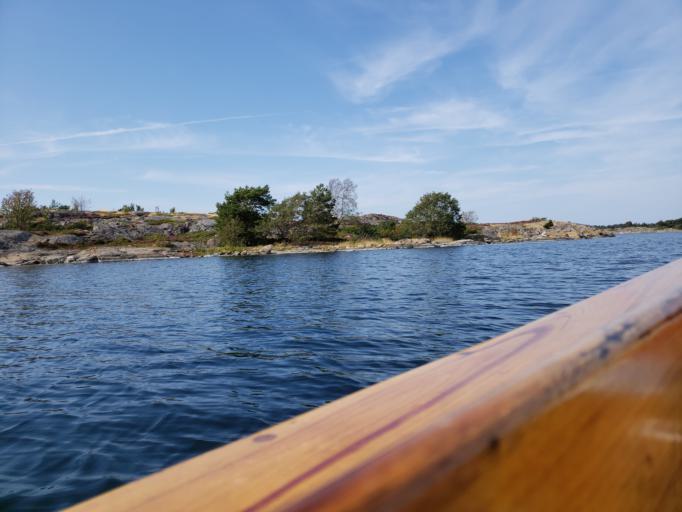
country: FI
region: Varsinais-Suomi
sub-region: Aboland-Turunmaa
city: Dragsfjaerd
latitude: 59.8441
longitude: 22.2061
